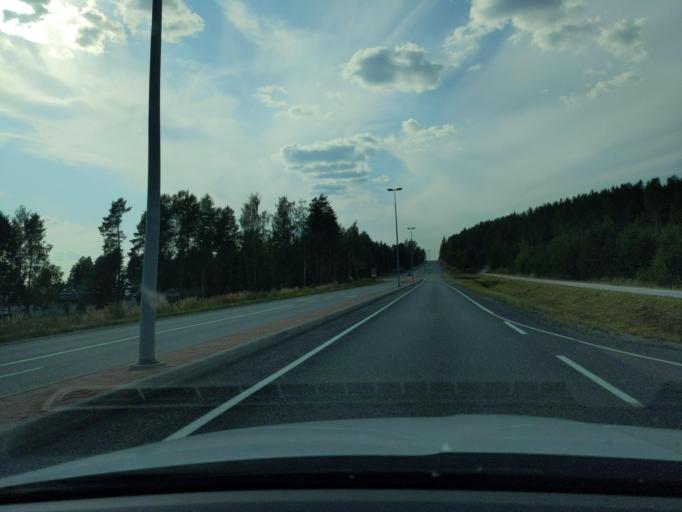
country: FI
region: Paijanne Tavastia
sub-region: Lahti
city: Asikkala
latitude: 61.1613
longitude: 25.5781
